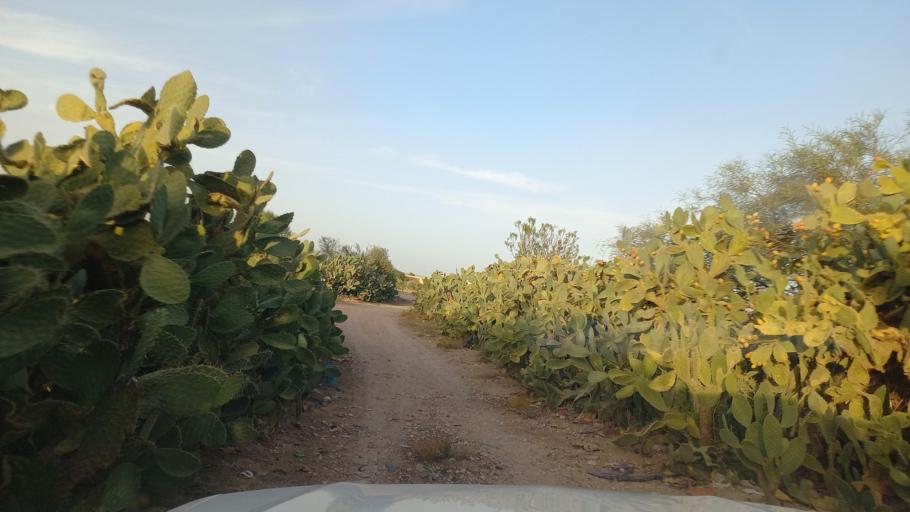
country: TN
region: Al Qasrayn
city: Kasserine
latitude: 35.2399
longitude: 8.9898
